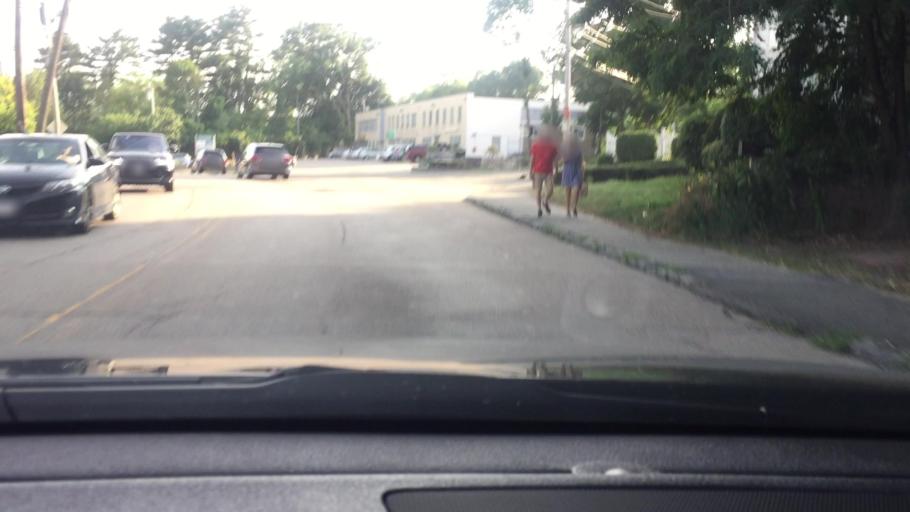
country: US
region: Massachusetts
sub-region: Middlesex County
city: Newton
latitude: 42.3188
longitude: -71.2079
